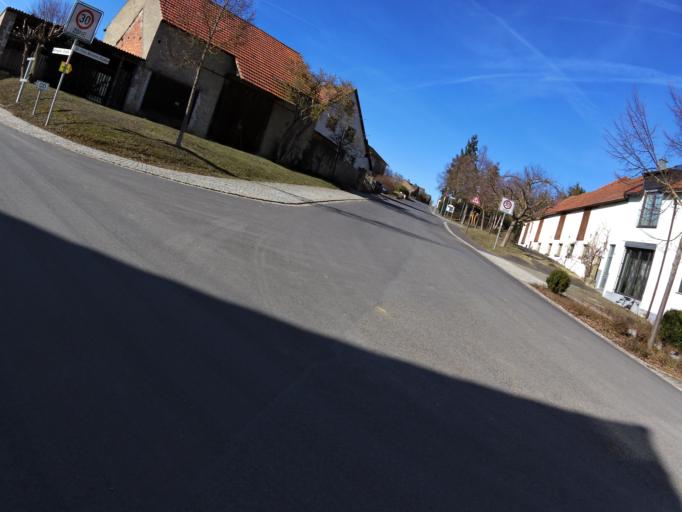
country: DE
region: Bavaria
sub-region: Regierungsbezirk Unterfranken
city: Kurnach
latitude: 49.8584
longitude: 10.0102
